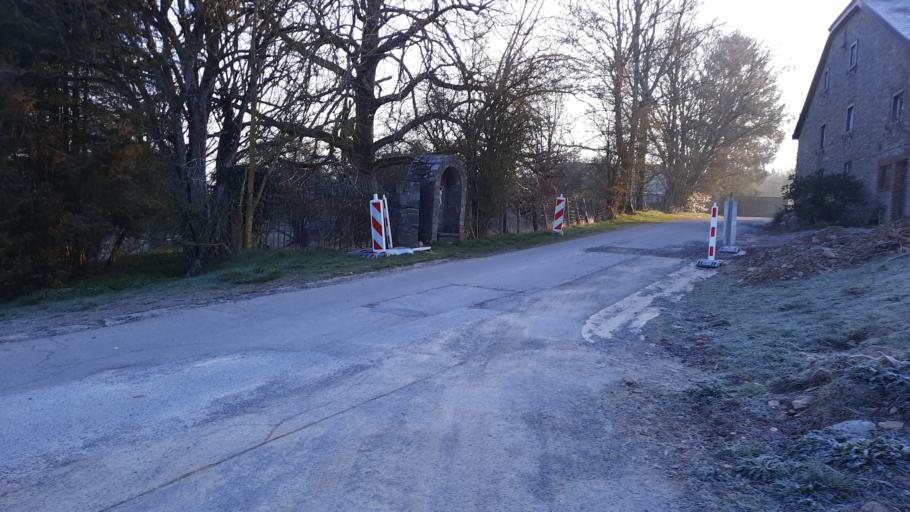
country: BE
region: Wallonia
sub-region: Province du Luxembourg
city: Manhay
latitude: 50.2795
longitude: 5.7153
